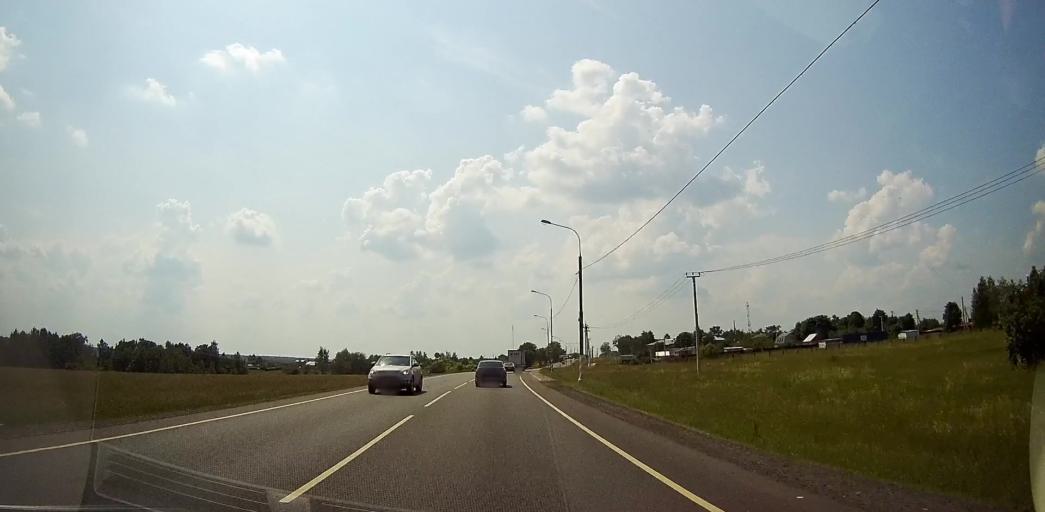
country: RU
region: Moskovskaya
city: Meshcherino
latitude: 55.1478
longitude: 38.2960
